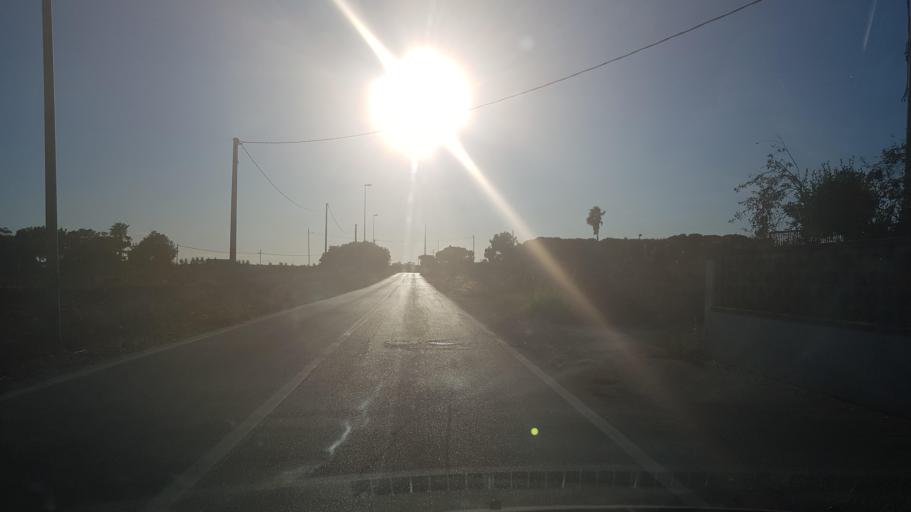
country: IT
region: Apulia
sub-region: Provincia di Lecce
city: Struda
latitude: 40.3266
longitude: 18.3147
